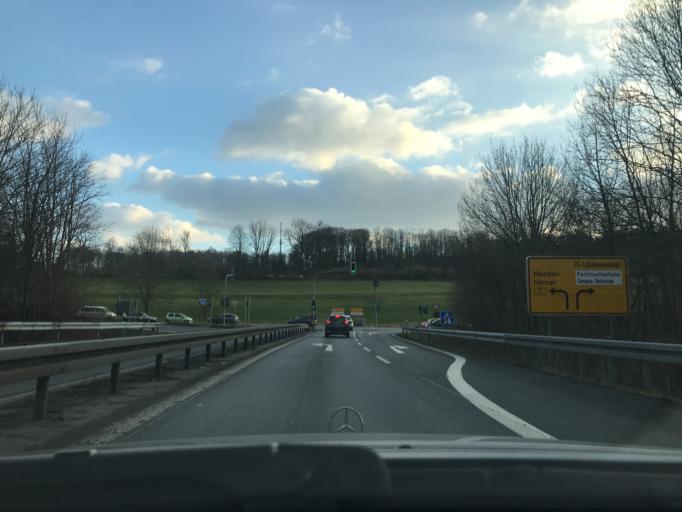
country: DE
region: North Rhine-Westphalia
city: Iserlohn
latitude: 51.3866
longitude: 7.7324
